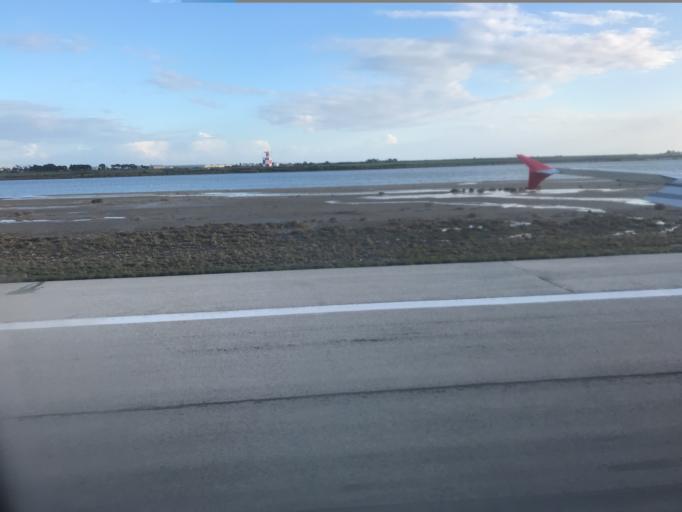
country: CY
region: Larnaka
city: Meneou
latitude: 34.8714
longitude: 33.6210
